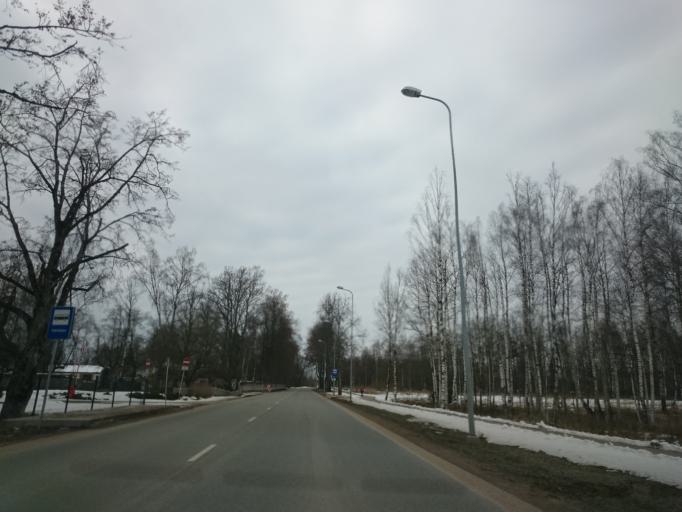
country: LV
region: Cesu Rajons
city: Cesis
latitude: 57.2955
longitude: 25.2636
